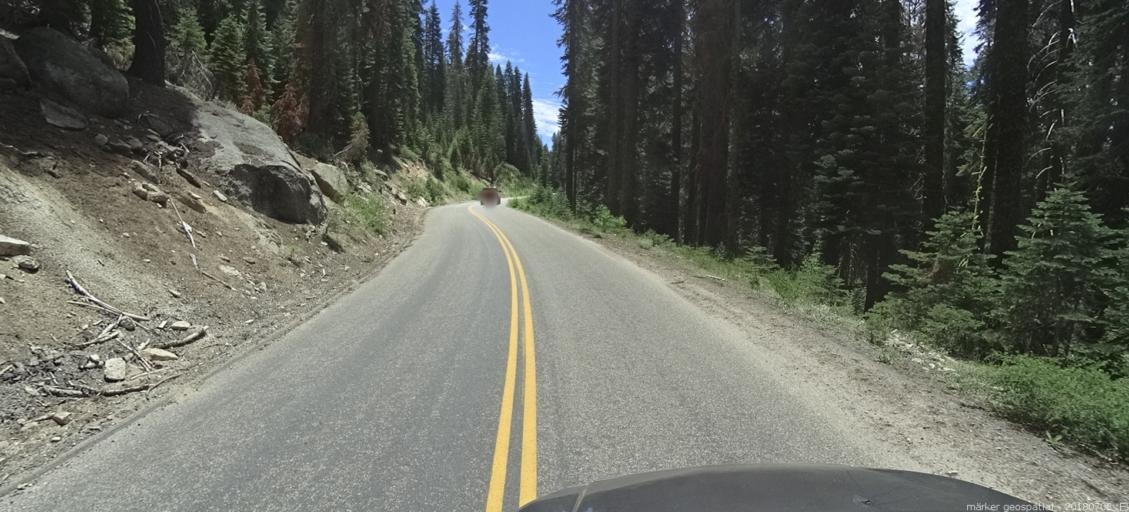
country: US
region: California
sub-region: Madera County
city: Oakhurst
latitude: 37.4262
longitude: -119.4874
